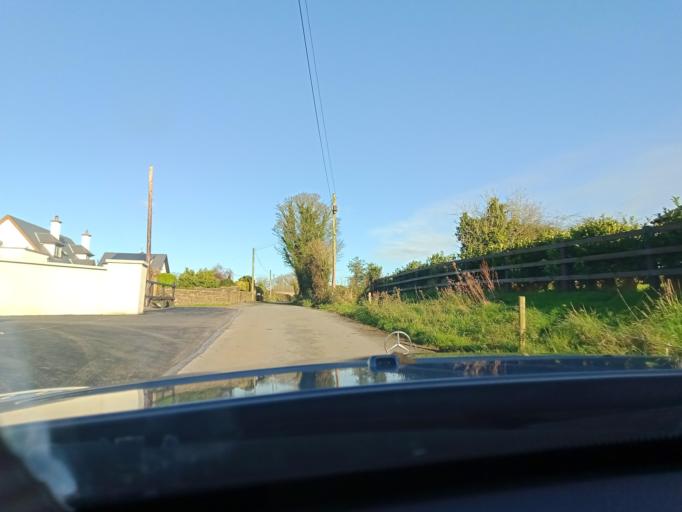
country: IE
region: Leinster
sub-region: Kilkenny
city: Mooncoin
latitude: 52.2676
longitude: -7.2384
